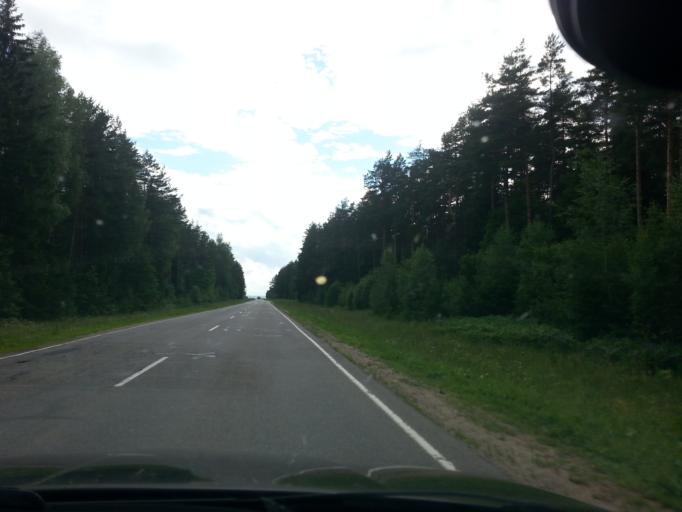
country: BY
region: Grodnenskaya
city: Astravyets
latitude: 54.7914
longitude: 26.0878
